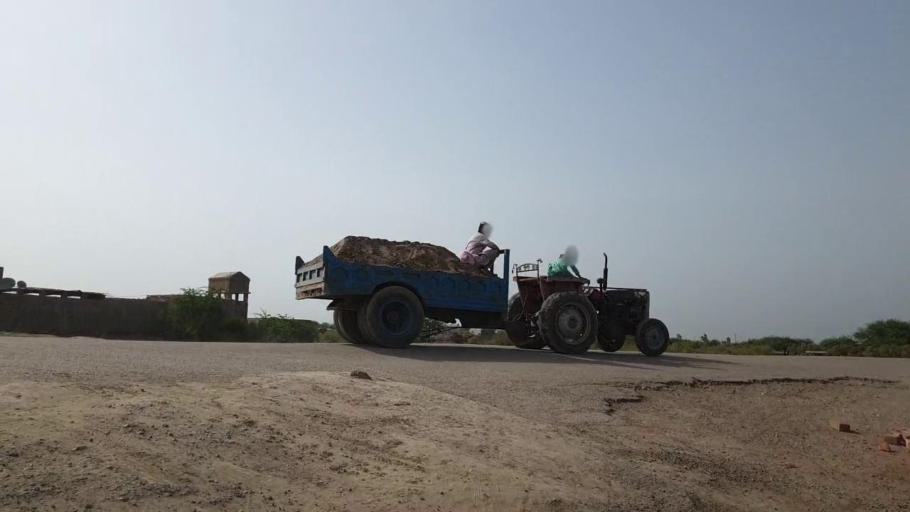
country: PK
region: Sindh
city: Jam Sahib
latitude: 26.2961
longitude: 68.6359
